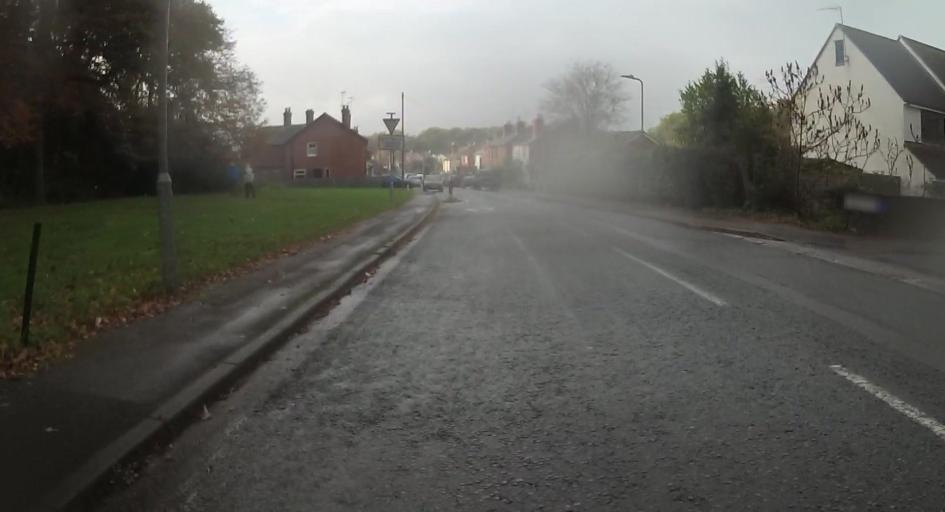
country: GB
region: England
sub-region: Bracknell Forest
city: Crowthorne
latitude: 51.3705
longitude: -0.7853
